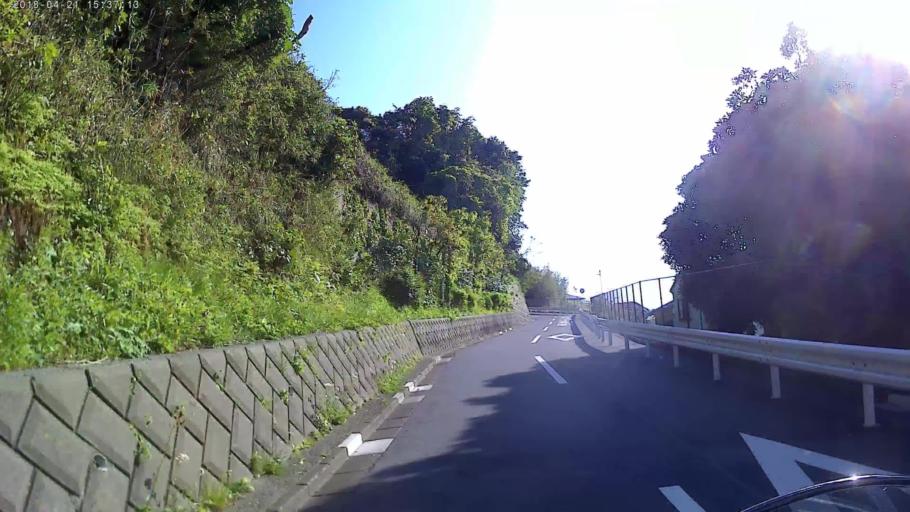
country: JP
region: Kanagawa
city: Fujisawa
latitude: 35.3205
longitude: 139.5068
